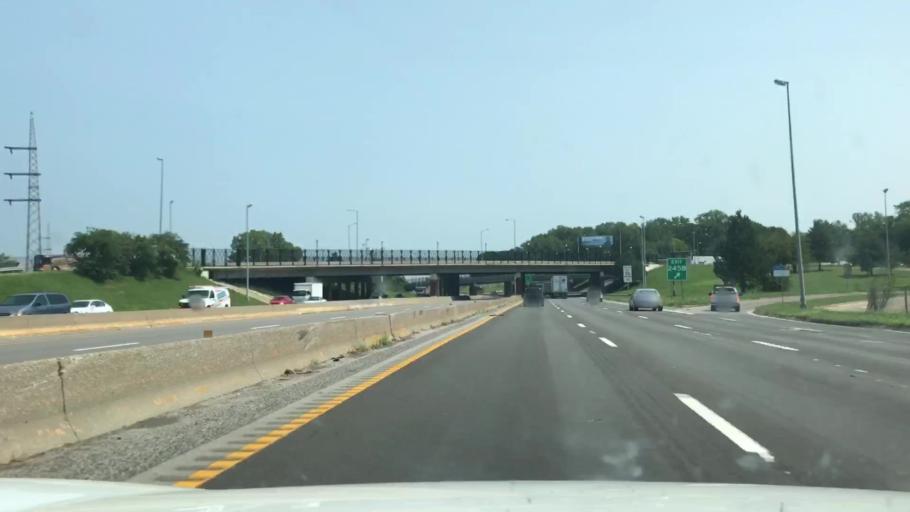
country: US
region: Missouri
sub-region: Saint Louis County
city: Pine Lawn
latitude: 38.6829
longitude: -90.2299
